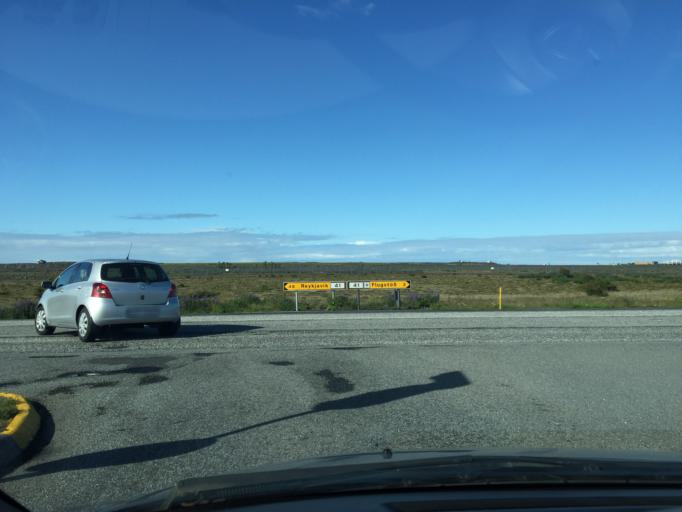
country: IS
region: Southern Peninsula
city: Reykjanesbaer
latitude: 63.9973
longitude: -22.5888
